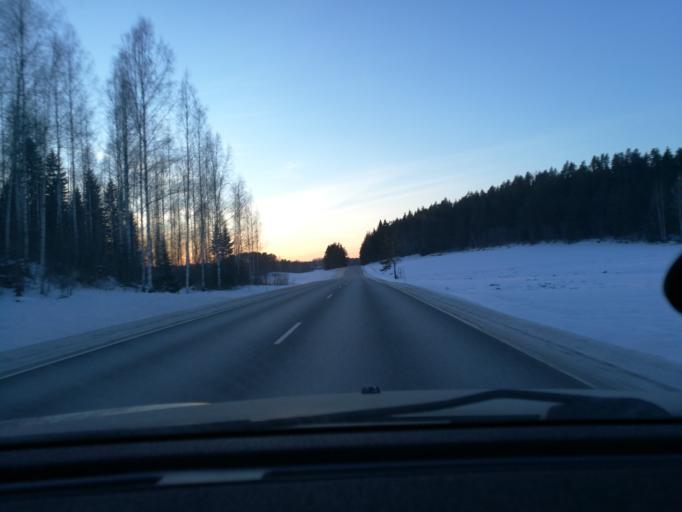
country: FI
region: Uusimaa
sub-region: Helsinki
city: Vihti
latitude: 60.4362
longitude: 24.4115
